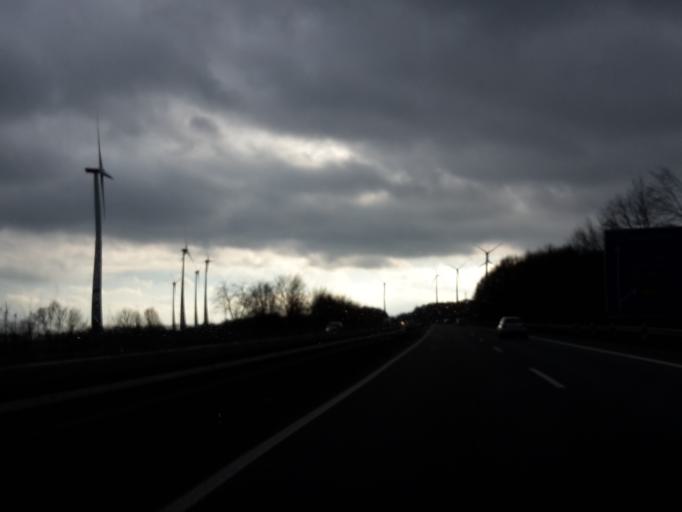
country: DE
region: Rheinland-Pfalz
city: Ober-Saulheim
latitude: 49.8501
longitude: 8.1477
